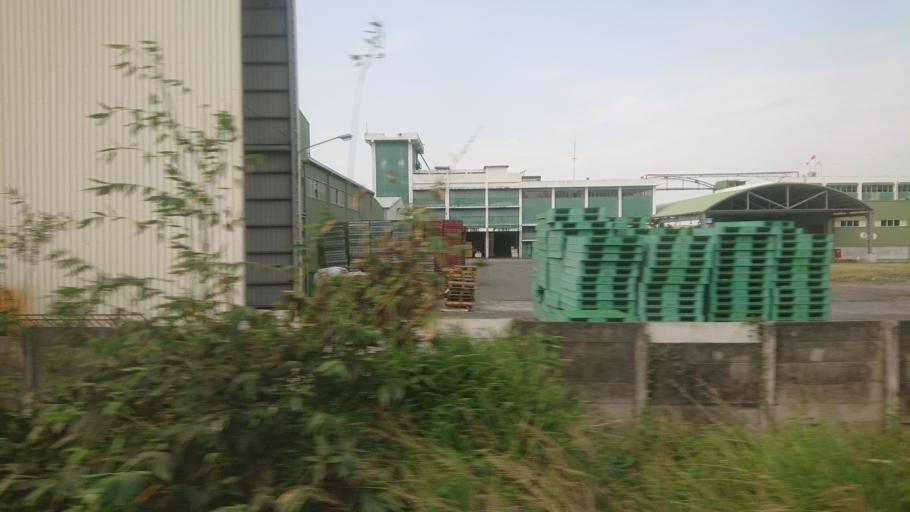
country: TW
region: Taiwan
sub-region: Nantou
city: Nantou
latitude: 23.8491
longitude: 120.5953
